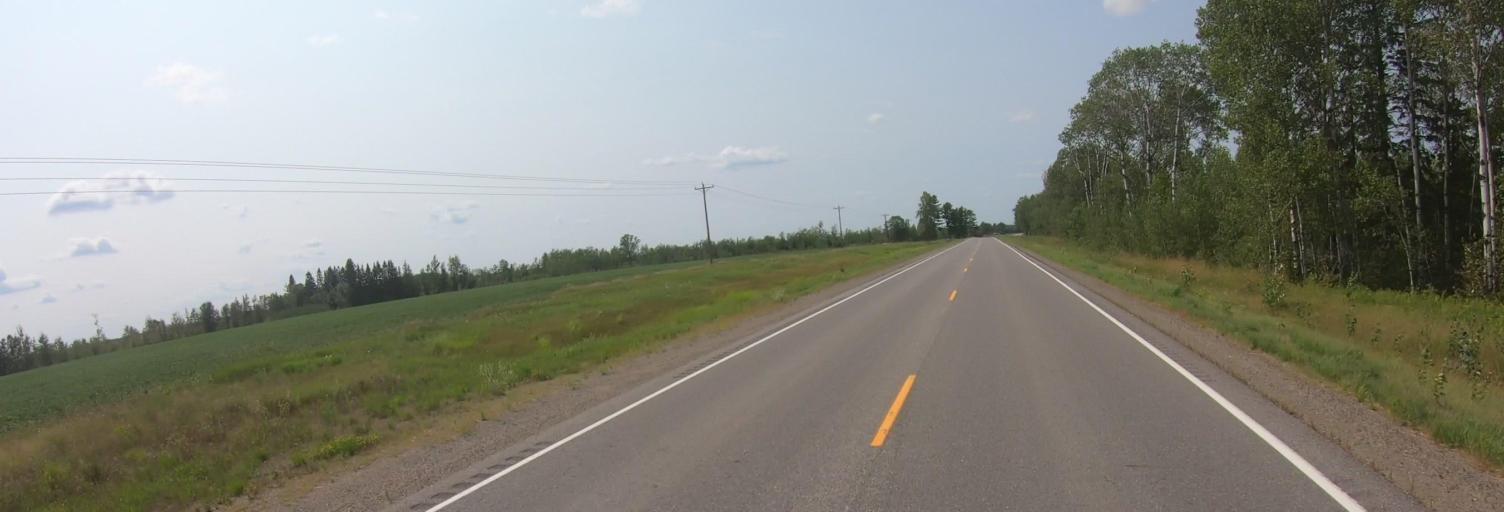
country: US
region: Minnesota
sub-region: Lake of the Woods County
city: Baudette
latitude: 48.6480
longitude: -94.2092
